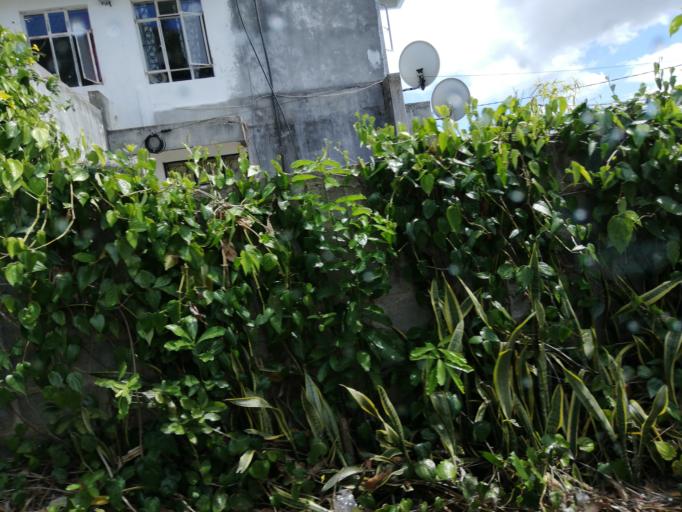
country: MU
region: Moka
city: Moka
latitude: -20.2139
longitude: 57.4733
